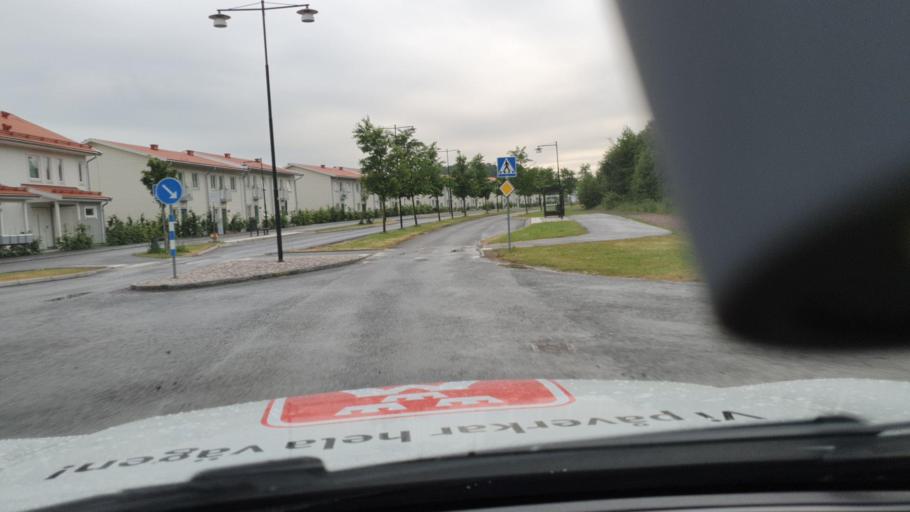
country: SE
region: Vaestra Goetaland
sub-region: Skovde Kommun
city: Stopen
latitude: 58.4168
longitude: 13.8991
